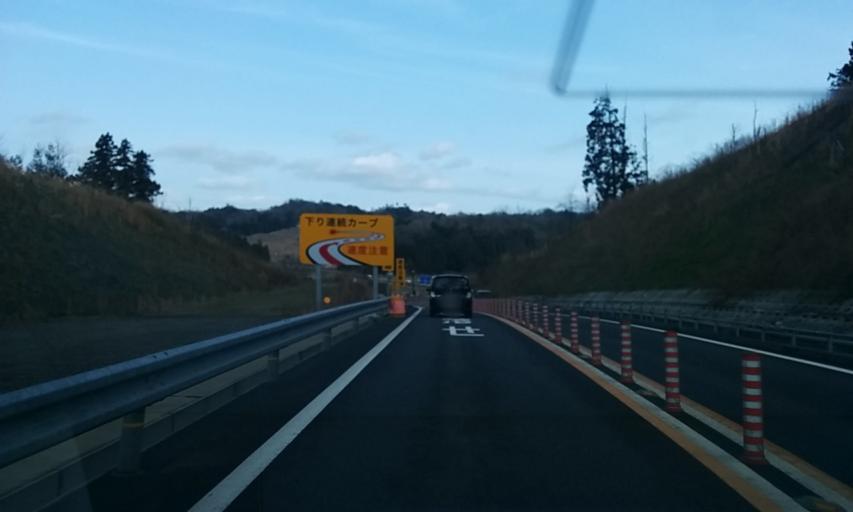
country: JP
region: Kyoto
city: Miyazu
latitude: 35.5736
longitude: 135.1214
